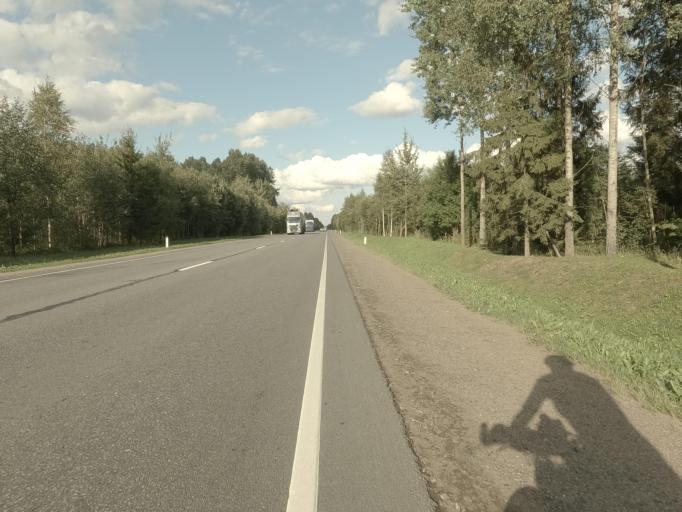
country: RU
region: Leningrad
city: Mga
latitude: 59.6844
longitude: 30.9585
